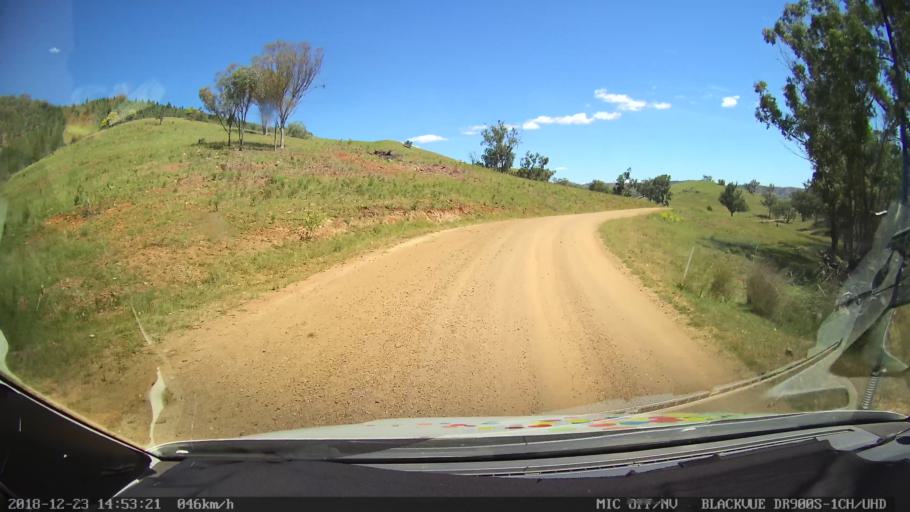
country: AU
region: New South Wales
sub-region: Tamworth Municipality
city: Manilla
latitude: -30.6908
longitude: 150.8517
